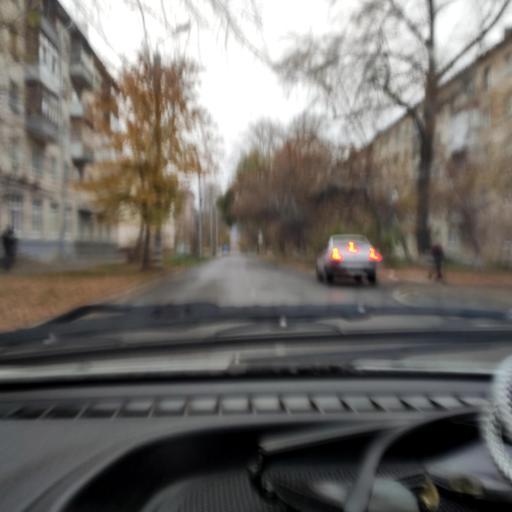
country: RU
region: Samara
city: Zhigulevsk
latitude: 53.4668
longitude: 49.5292
